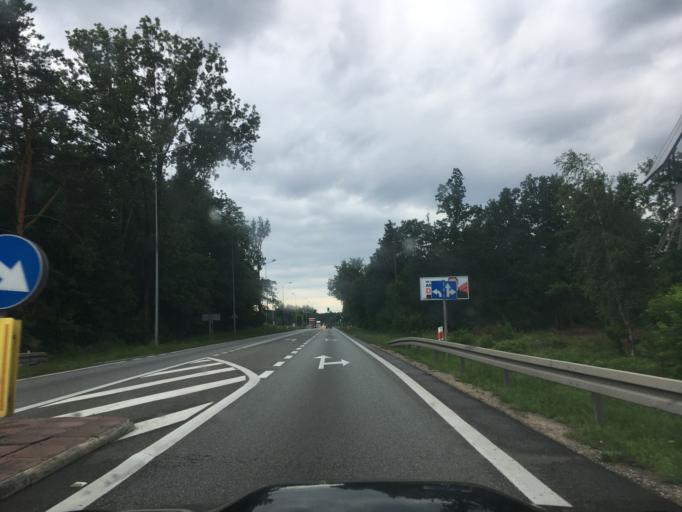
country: PL
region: Masovian Voivodeship
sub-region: Powiat otwocki
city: Celestynow
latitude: 52.0413
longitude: 21.3883
